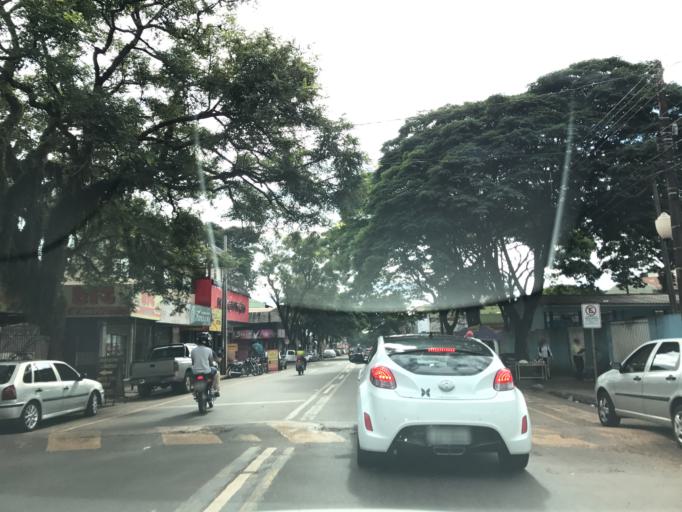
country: BR
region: Parana
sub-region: Sarandi
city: Sarandi
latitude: -23.4387
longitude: -51.8709
